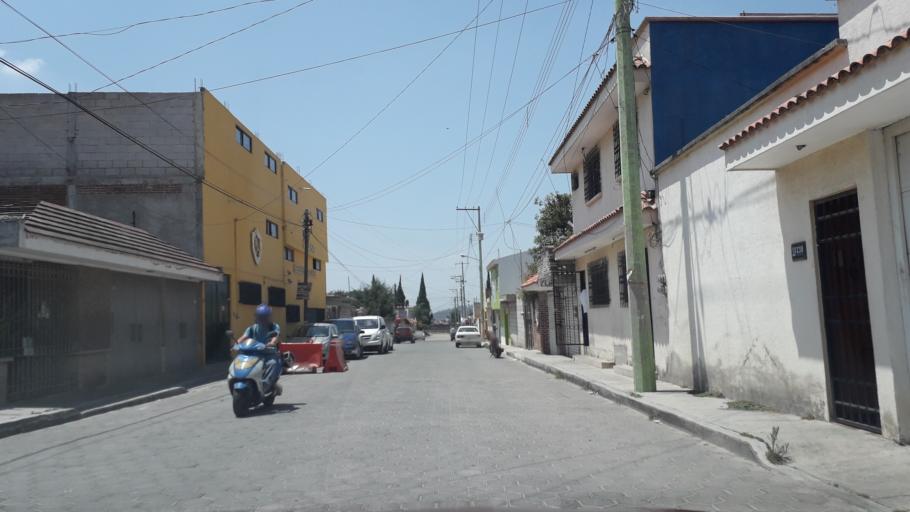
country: MX
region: Puebla
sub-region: Puebla
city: Primero de Mayo
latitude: 19.0696
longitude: -98.1191
